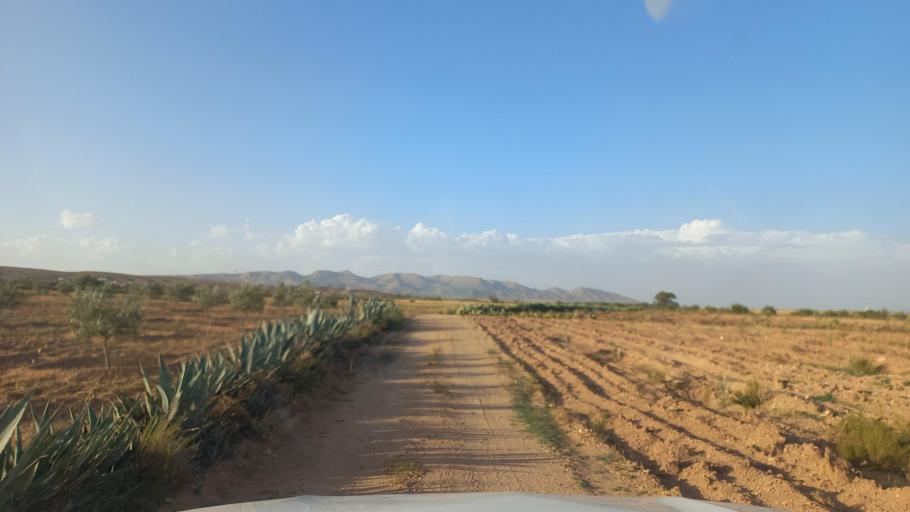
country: TN
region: Al Qasrayn
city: Sbiba
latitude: 35.3640
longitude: 9.0212
